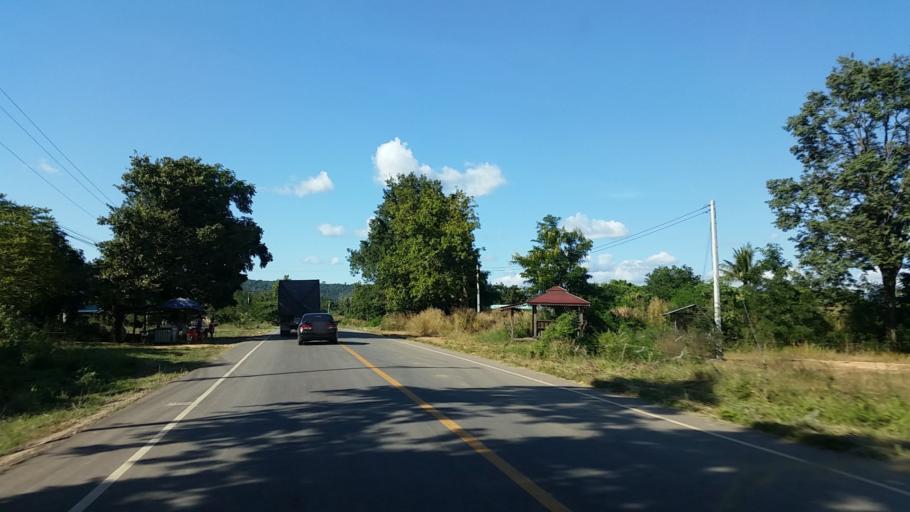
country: TH
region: Chaiyaphum
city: Thep Sathit
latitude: 15.5497
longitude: 101.4371
